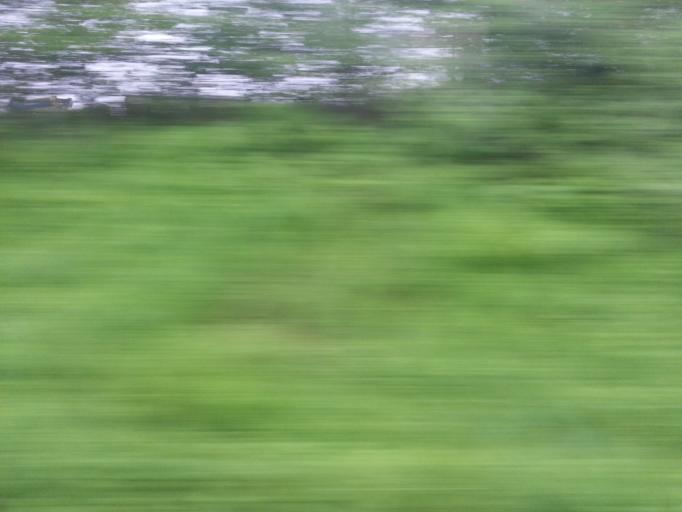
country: NO
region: Sor-Trondelag
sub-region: Melhus
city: Melhus
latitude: 63.3424
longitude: 10.3444
